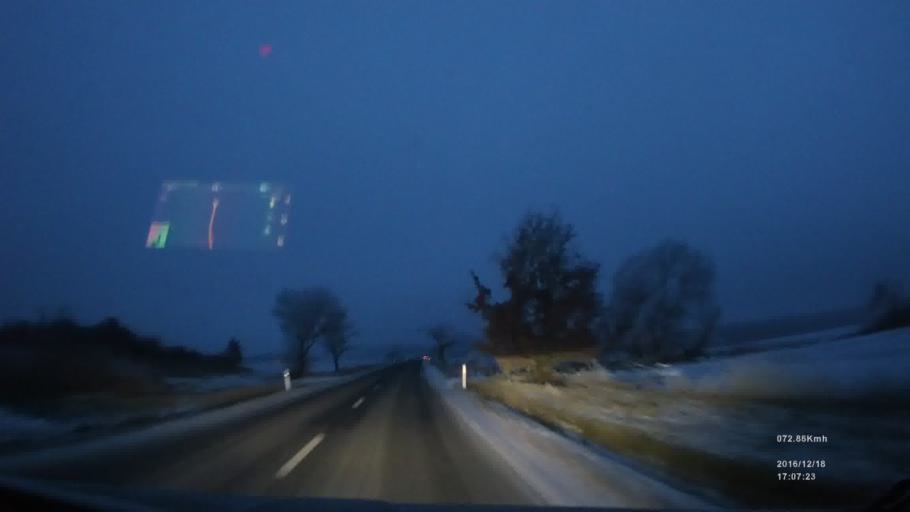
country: SK
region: Presovsky
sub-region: Okres Presov
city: Presov
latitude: 48.8970
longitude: 21.3207
